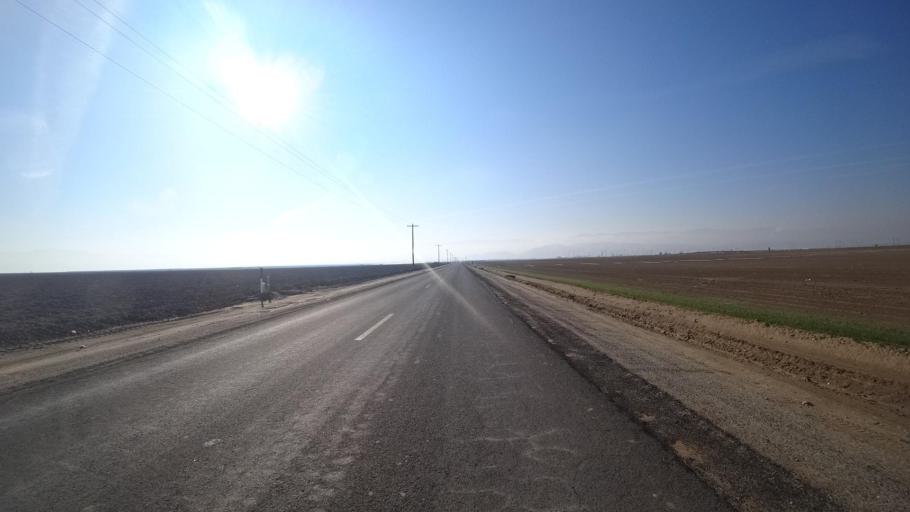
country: US
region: California
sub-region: Kern County
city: Weedpatch
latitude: 35.1069
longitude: -118.9677
